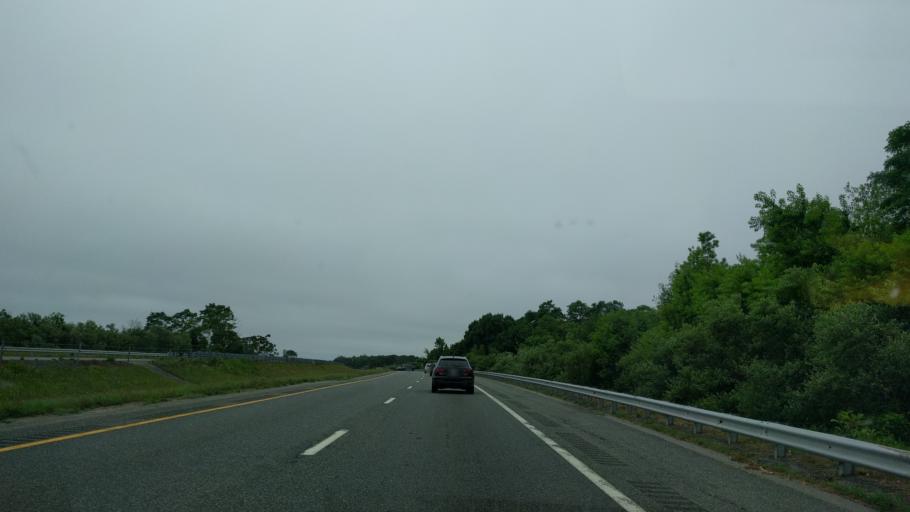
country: US
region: Rhode Island
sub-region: Washington County
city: Exeter
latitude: 41.6041
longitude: -71.4980
